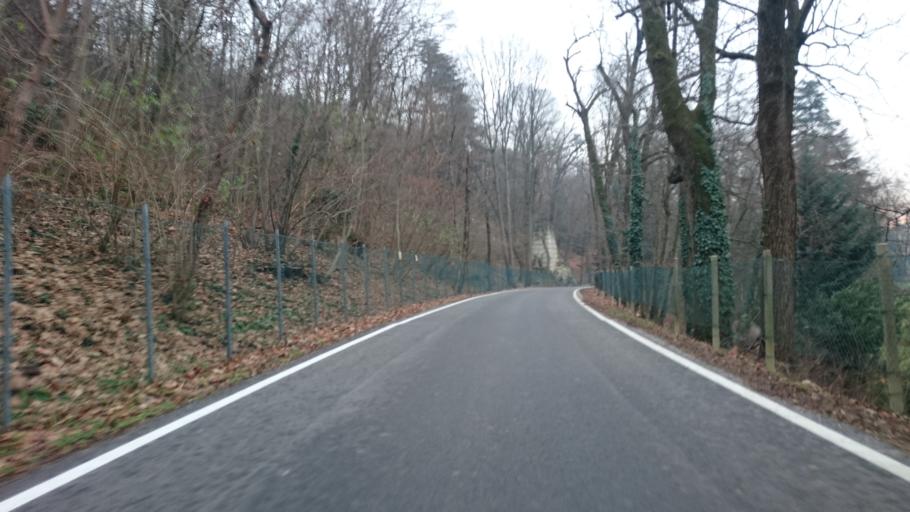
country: IT
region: Veneto
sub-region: Provincia di Vicenza
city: Montegalda
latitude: 45.4530
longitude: 11.6679
